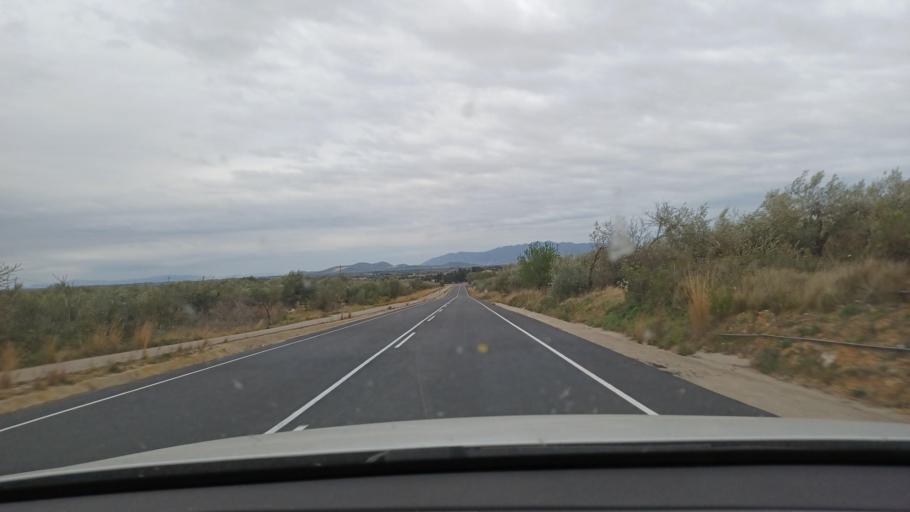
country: ES
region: Valencia
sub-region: Provincia de Castello
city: Traiguera
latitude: 40.5309
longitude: 0.2982
